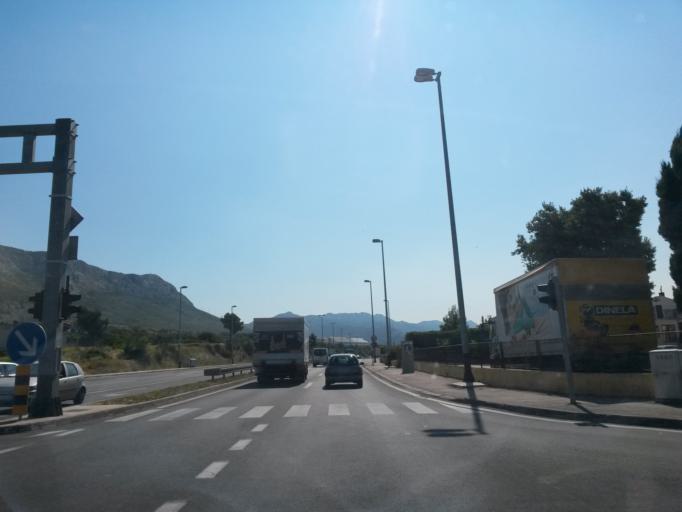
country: HR
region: Splitsko-Dalmatinska
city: Vranjic
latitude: 43.5510
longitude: 16.4290
